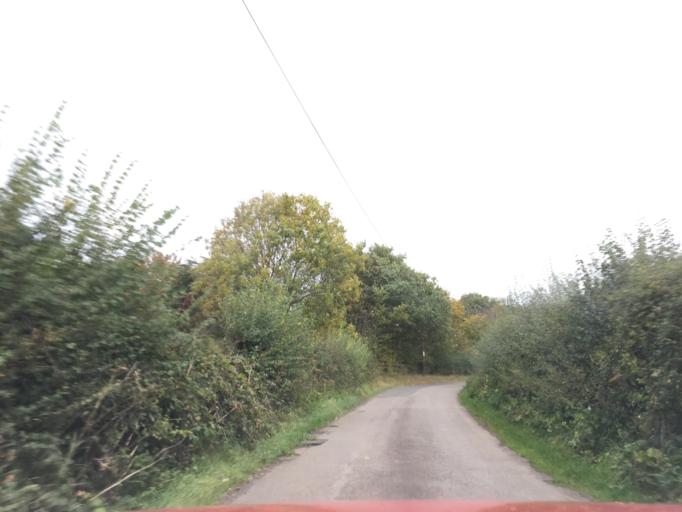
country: GB
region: England
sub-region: Gloucestershire
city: Stonehouse
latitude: 51.7532
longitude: -2.3069
